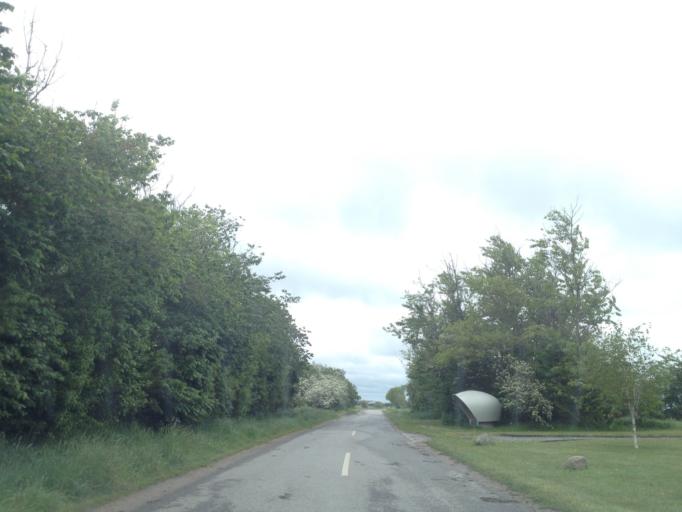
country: DK
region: South Denmark
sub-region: Tonder Kommune
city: Sherrebek
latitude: 55.0985
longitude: 8.7431
